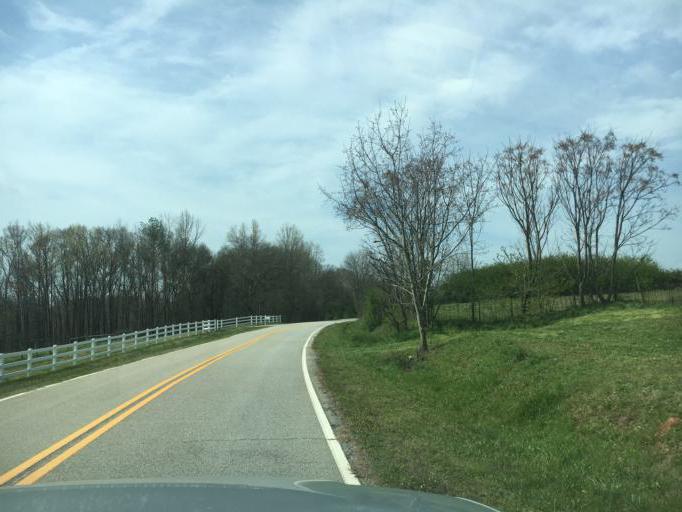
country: US
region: Georgia
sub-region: Franklin County
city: Lavonia
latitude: 34.4366
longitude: -83.0390
